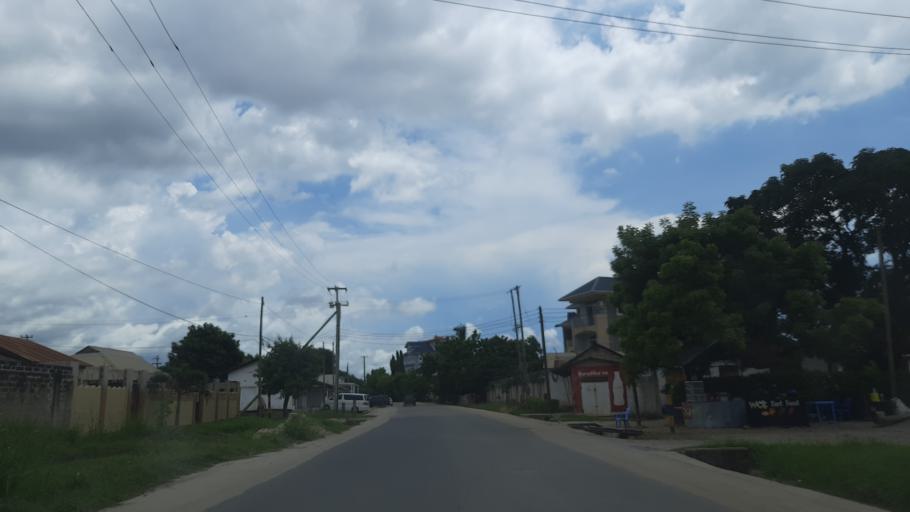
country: TZ
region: Dar es Salaam
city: Magomeni
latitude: -6.7806
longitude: 39.2389
